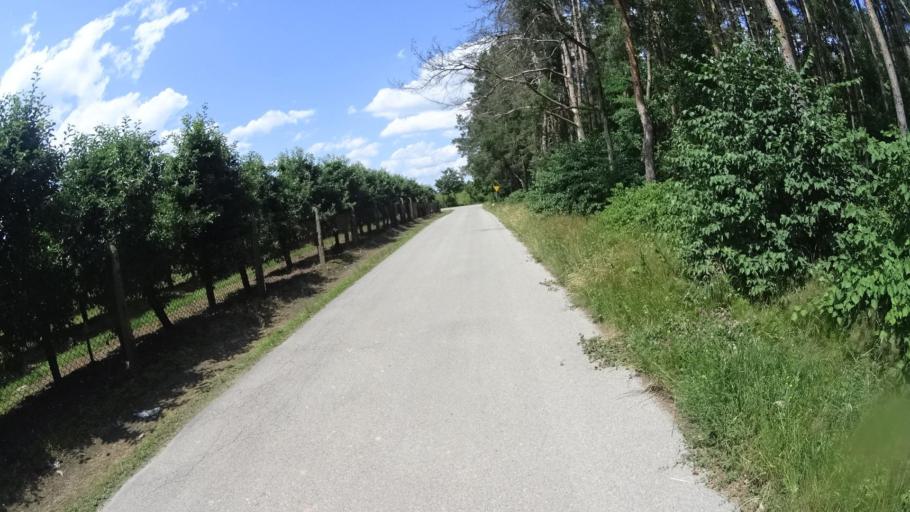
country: PL
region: Masovian Voivodeship
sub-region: Powiat grojecki
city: Goszczyn
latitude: 51.7156
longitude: 20.8989
